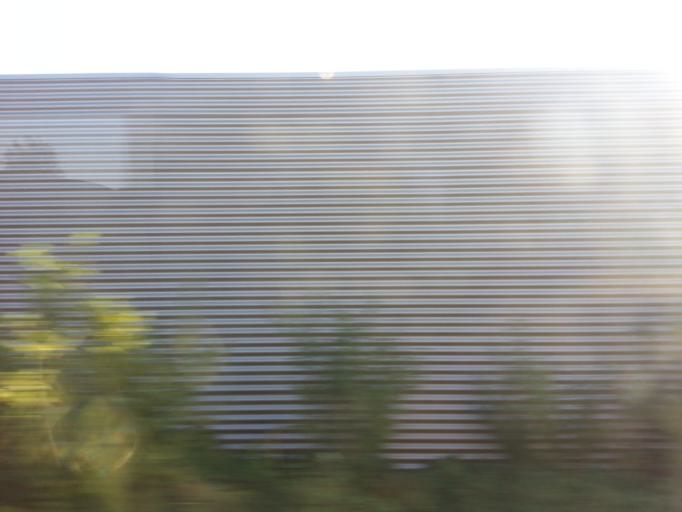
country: NL
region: North Brabant
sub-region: Gemeente Vught
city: Vught
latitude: 51.6462
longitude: 5.2933
